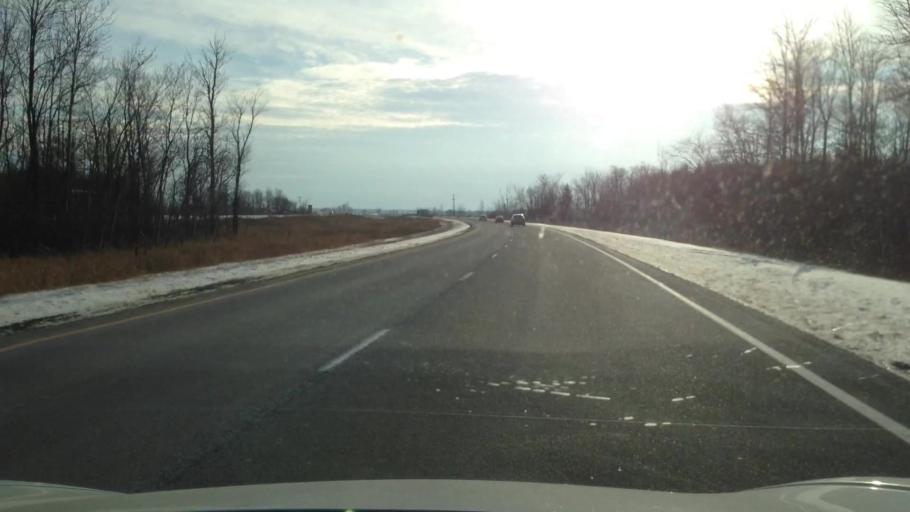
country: CA
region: Ontario
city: Casselman
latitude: 45.3582
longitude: -74.8846
